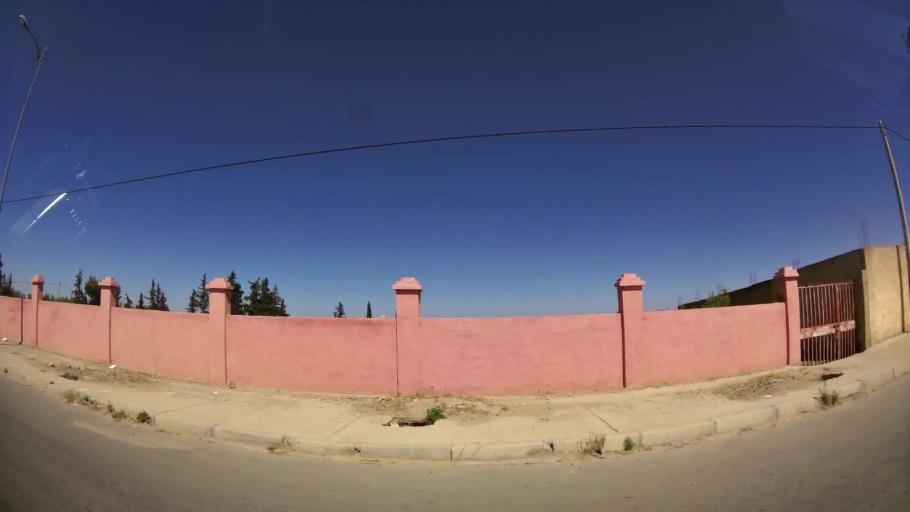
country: MA
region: Oriental
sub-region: Oujda-Angad
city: Oujda
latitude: 34.6956
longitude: -1.8573
